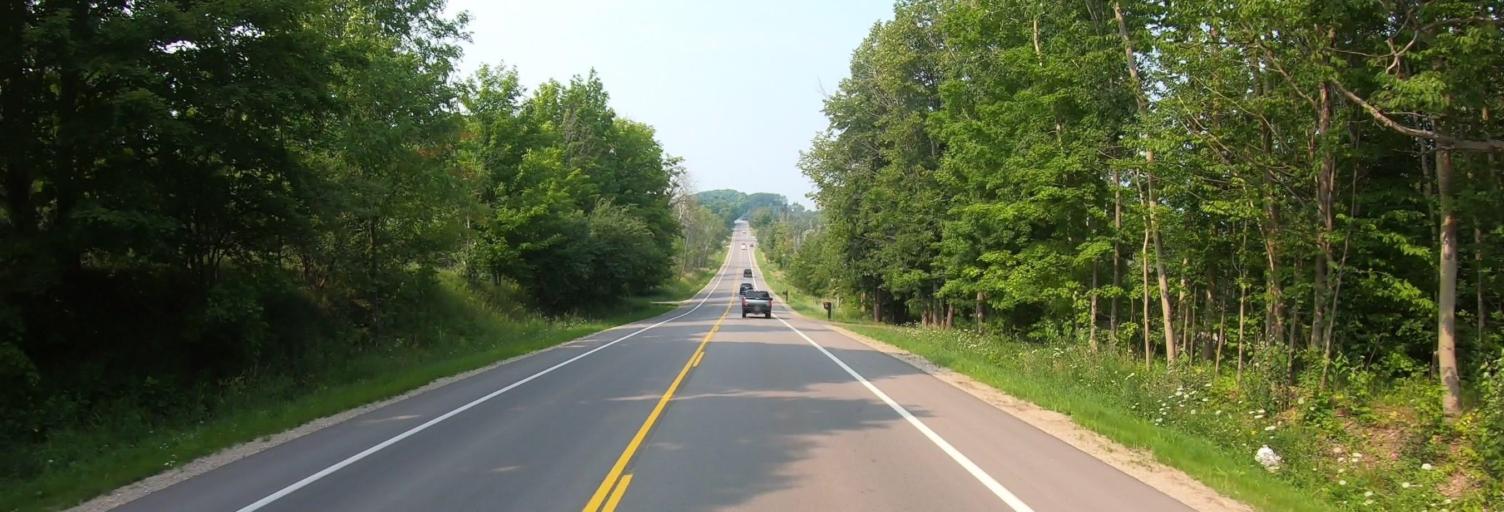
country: US
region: Michigan
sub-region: Charlevoix County
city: Charlevoix
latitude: 45.2480
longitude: -85.2612
